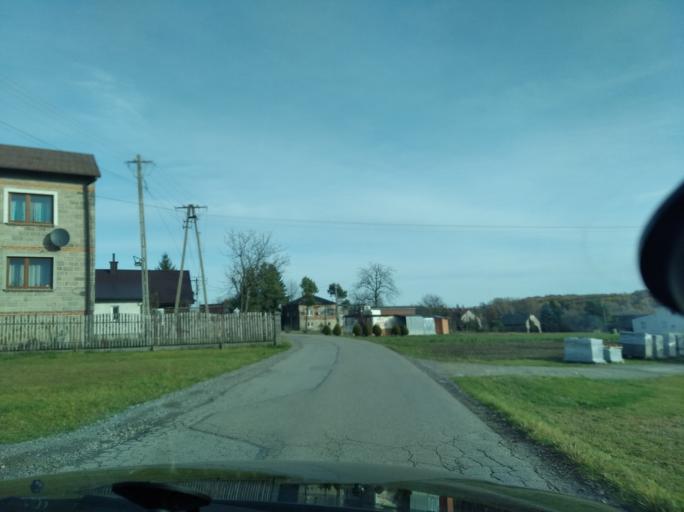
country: PL
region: Subcarpathian Voivodeship
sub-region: Powiat rzeszowski
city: Krasne
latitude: 50.0105
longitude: 22.0946
